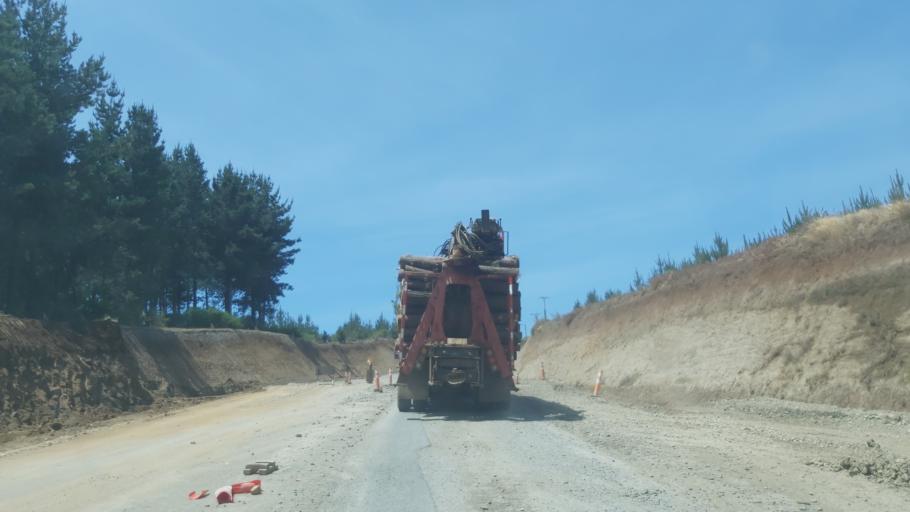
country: CL
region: Maule
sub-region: Provincia de Talca
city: Constitucion
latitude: -35.4489
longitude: -72.4751
